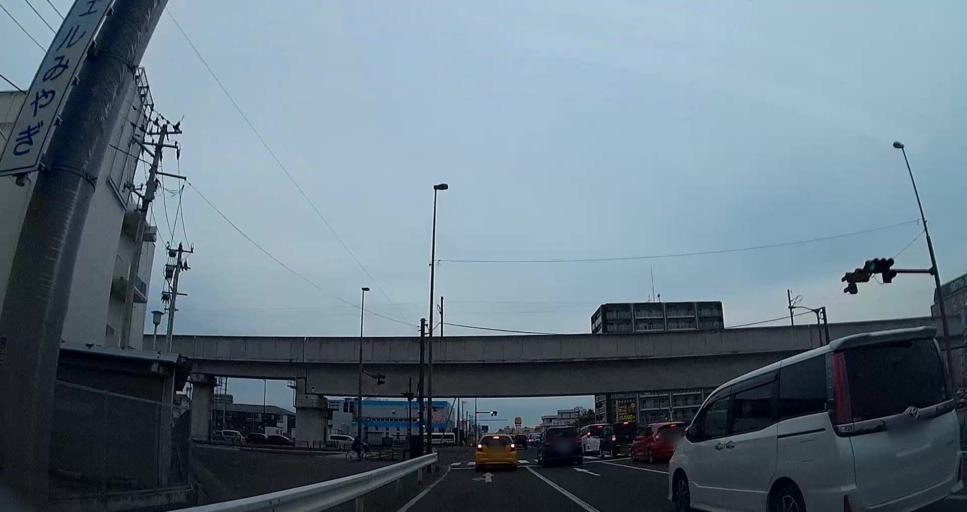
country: JP
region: Miyagi
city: Iwanuma
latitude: 38.1656
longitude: 140.8897
